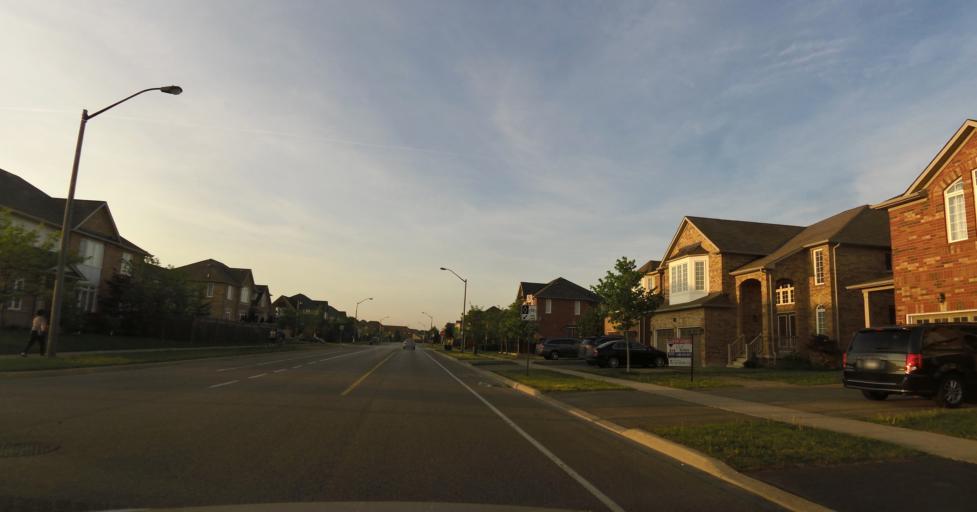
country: CA
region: Ontario
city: Oakville
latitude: 43.4450
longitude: -79.7608
